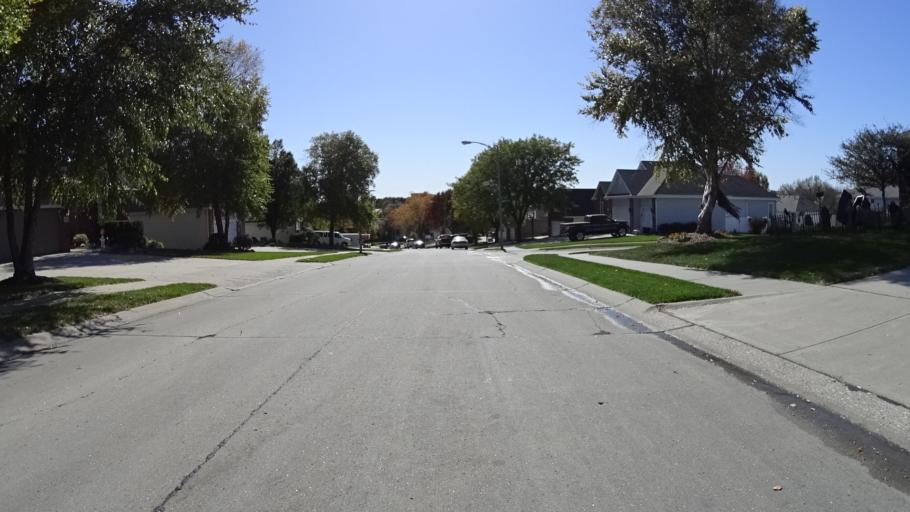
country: US
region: Nebraska
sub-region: Sarpy County
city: La Vista
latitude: 41.1717
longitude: -96.0246
